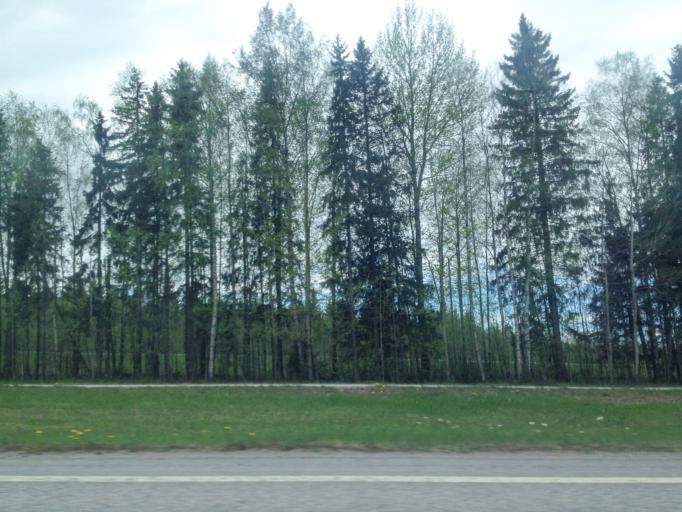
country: FI
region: Uusimaa
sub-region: Helsinki
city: Nurmijaervi
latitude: 60.5089
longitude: 24.8490
